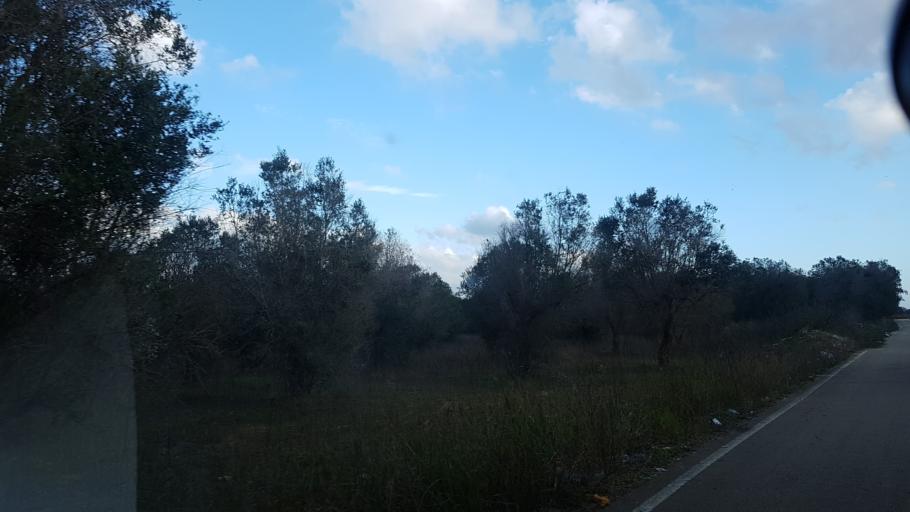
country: IT
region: Apulia
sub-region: Provincia di Brindisi
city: San Pietro Vernotico
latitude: 40.5139
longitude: 18.0153
